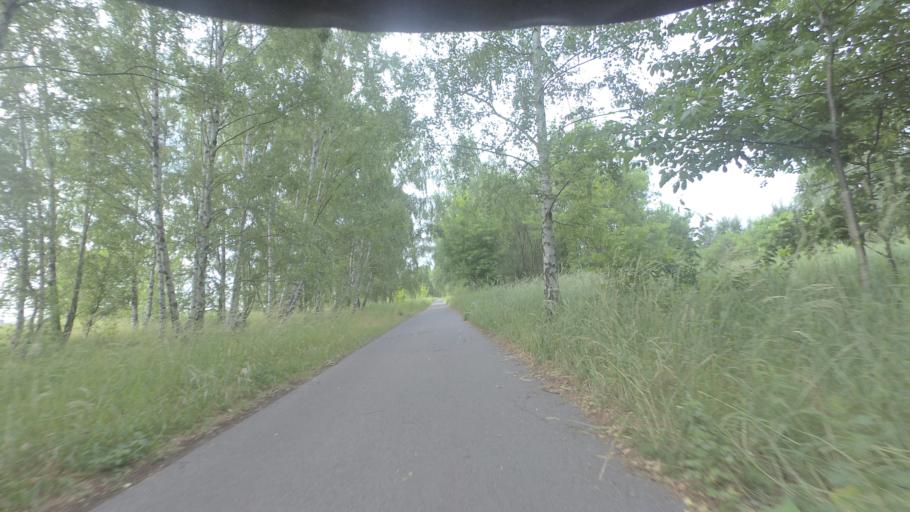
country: DE
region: Berlin
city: Gropiusstadt
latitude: 52.4132
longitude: 13.4704
